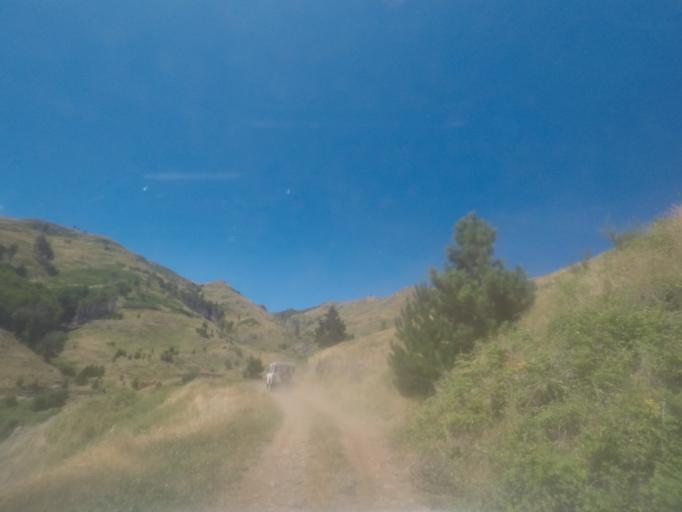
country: PT
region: Madeira
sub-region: Funchal
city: Nossa Senhora do Monte
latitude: 32.7037
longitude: -16.9012
